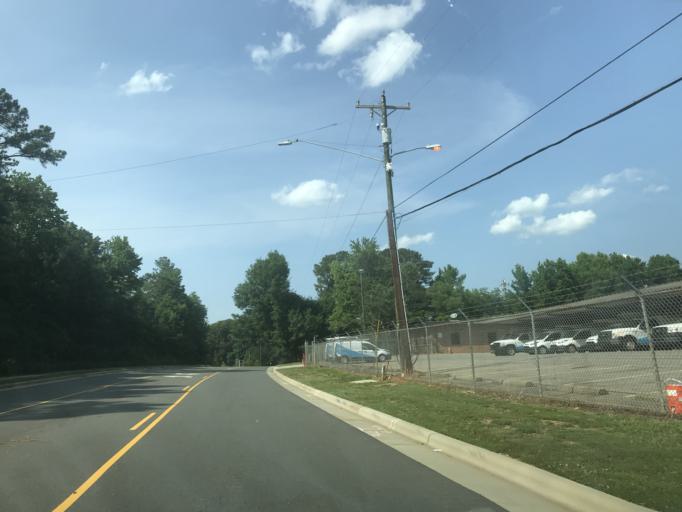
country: US
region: North Carolina
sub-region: Wake County
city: Cary
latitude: 35.7962
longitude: -78.7348
